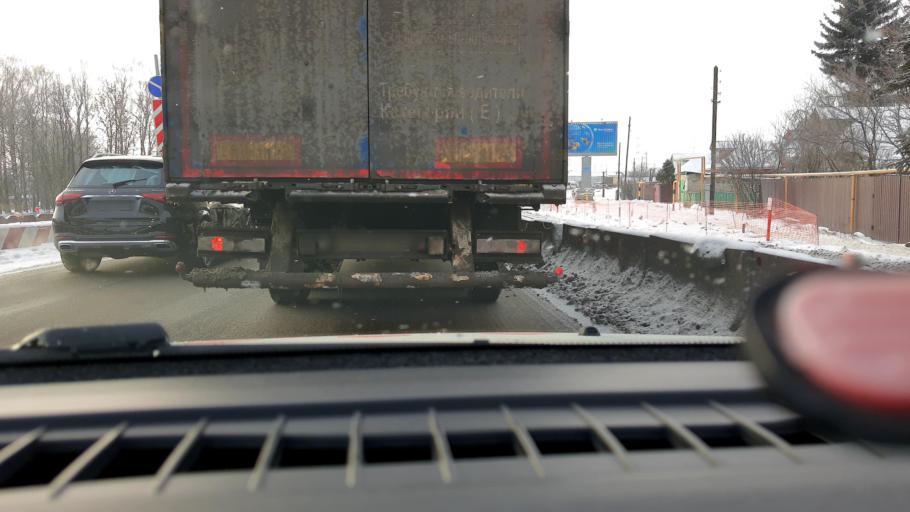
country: RU
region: Nizjnij Novgorod
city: Nizhniy Novgorod
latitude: 56.2184
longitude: 43.9343
